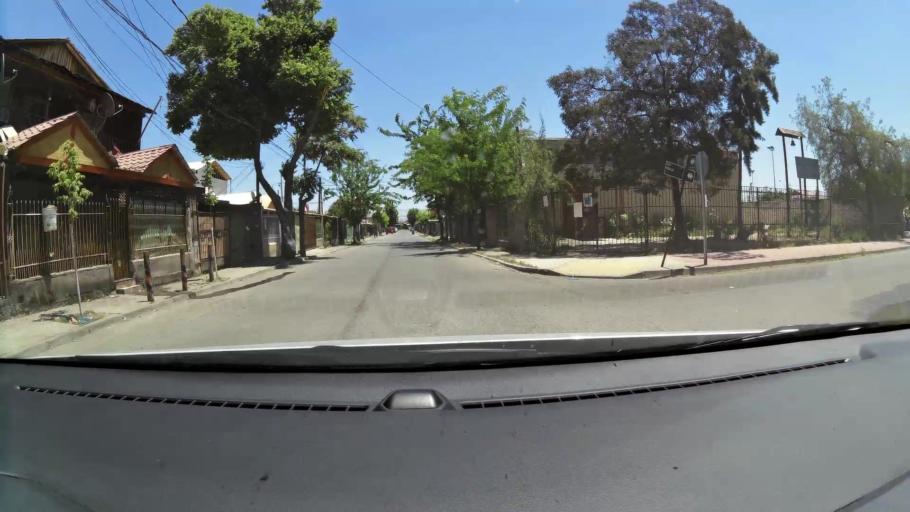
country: CL
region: Santiago Metropolitan
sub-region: Provincia de Maipo
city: San Bernardo
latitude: -33.5769
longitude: -70.6727
